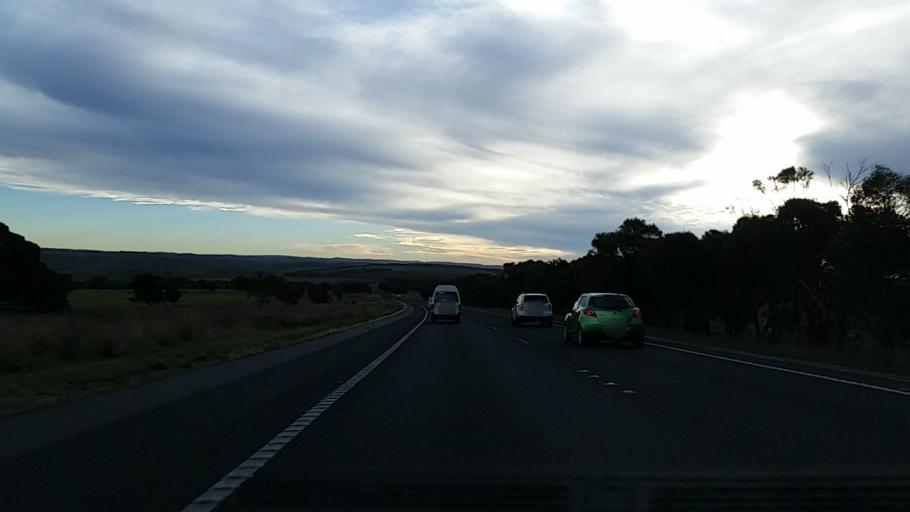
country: AU
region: South Australia
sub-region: Mount Barker
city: Callington
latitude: -35.1323
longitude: 139.0591
